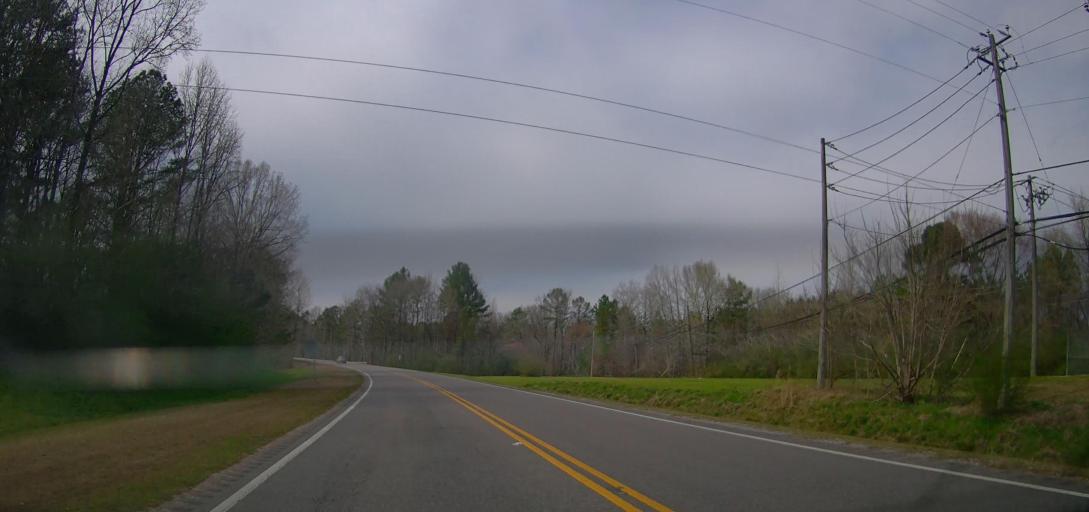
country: US
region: Alabama
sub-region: Walker County
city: Carbon Hill
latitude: 33.8967
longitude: -87.5374
